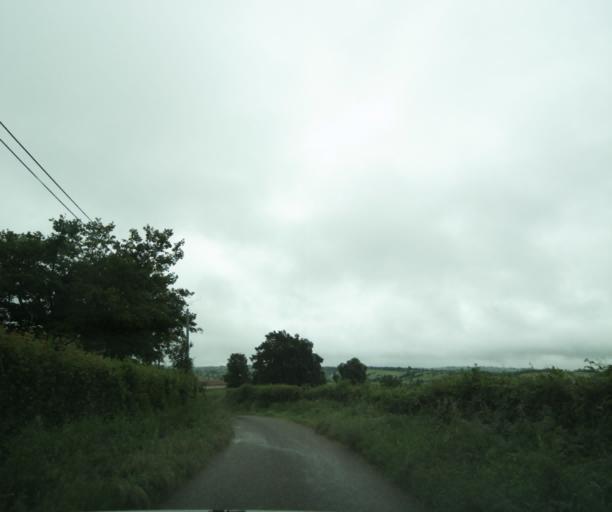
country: FR
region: Bourgogne
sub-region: Departement de Saone-et-Loire
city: La Clayette
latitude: 46.3509
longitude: 4.2302
